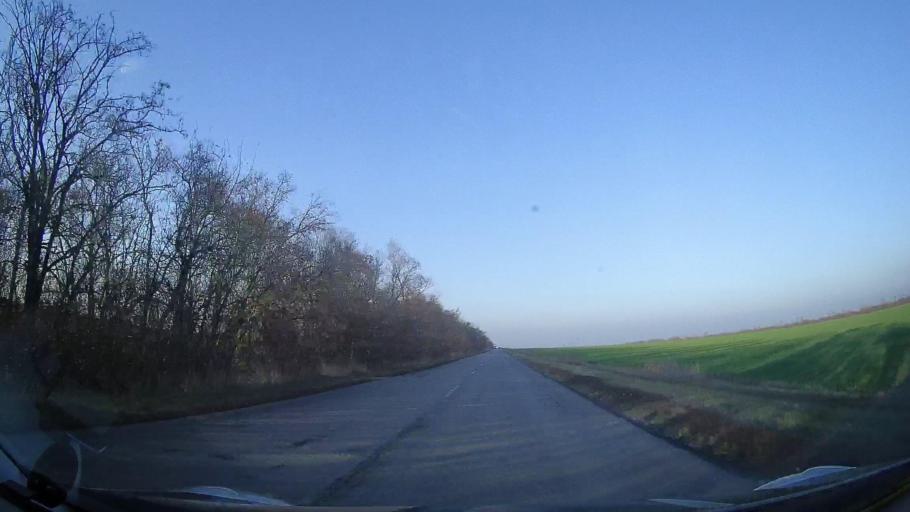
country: RU
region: Rostov
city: Kirovskaya
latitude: 47.0053
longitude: 39.9790
